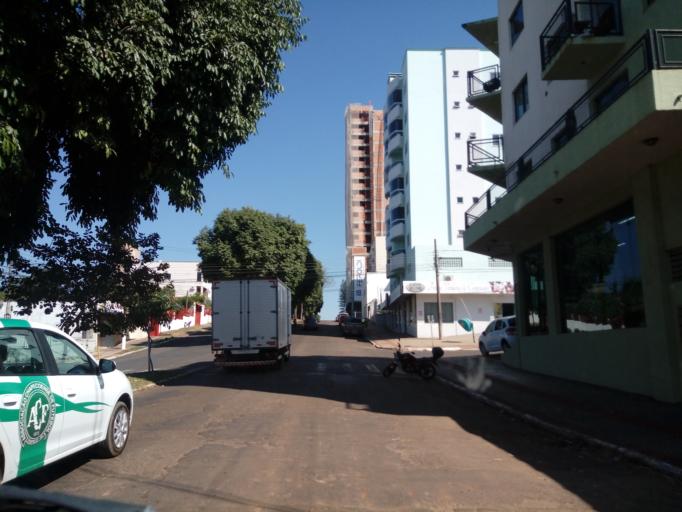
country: BR
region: Santa Catarina
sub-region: Chapeco
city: Chapeco
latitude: -27.0929
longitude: -52.6061
